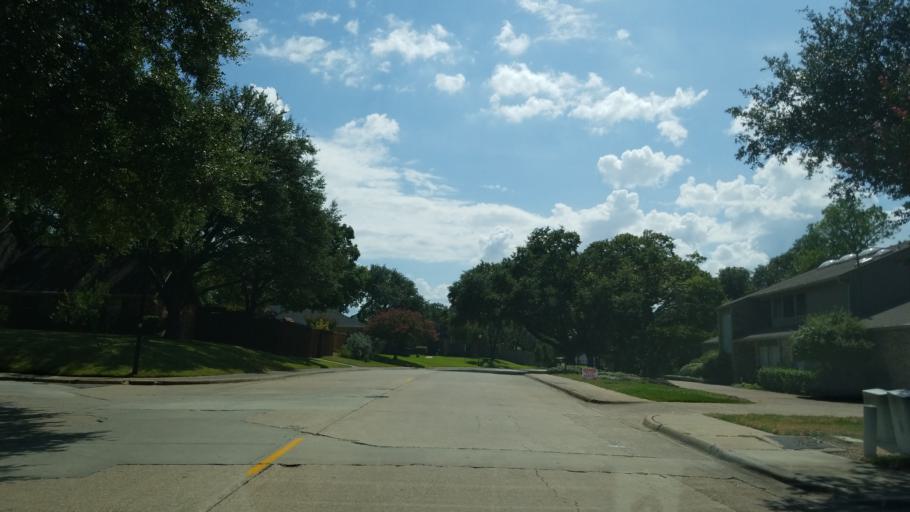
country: US
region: Texas
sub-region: Dallas County
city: Addison
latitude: 32.9534
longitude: -96.7913
